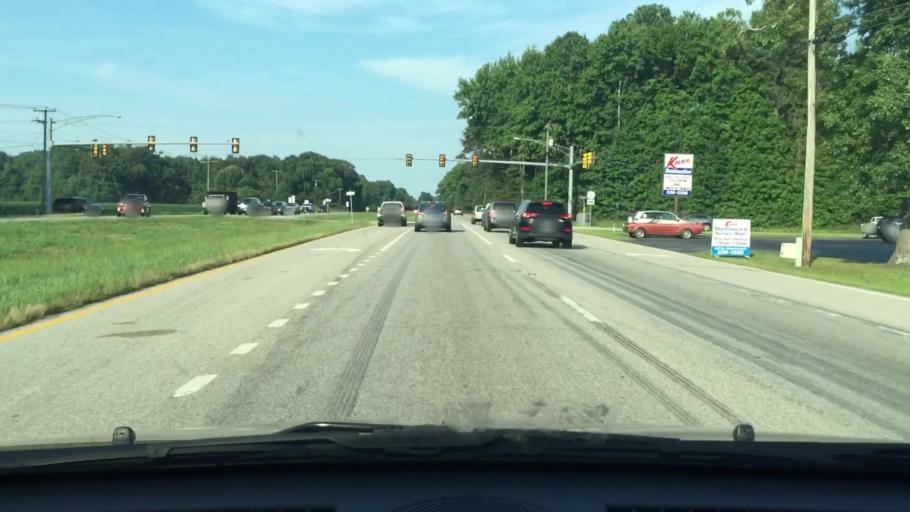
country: US
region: Virginia
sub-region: Isle of Wight County
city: Carrollton
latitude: 36.9432
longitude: -76.5559
